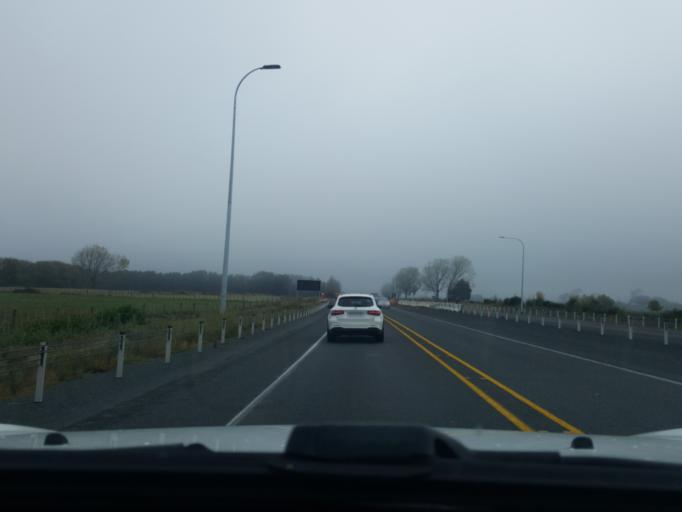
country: NZ
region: Waikato
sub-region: Waikato District
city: Te Kauwhata
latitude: -37.5032
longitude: 175.1649
